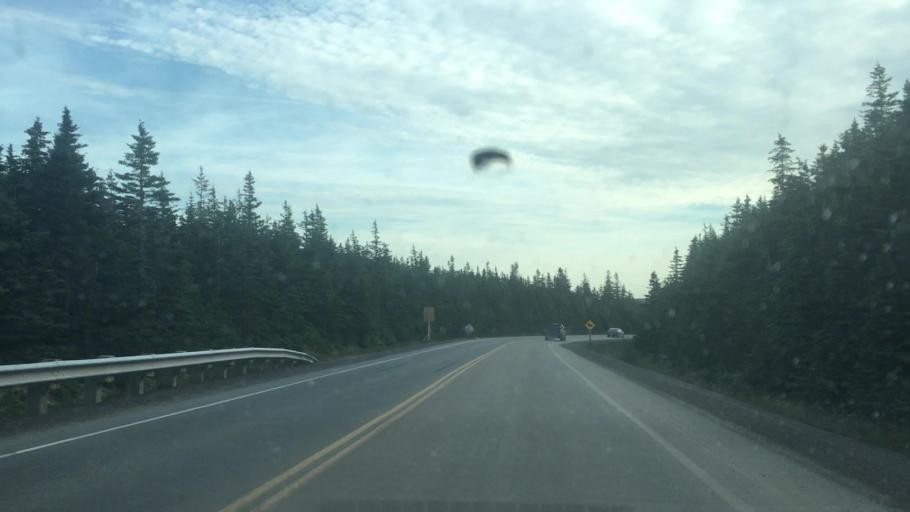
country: CA
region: Nova Scotia
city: Sydney Mines
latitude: 46.8005
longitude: -60.8442
